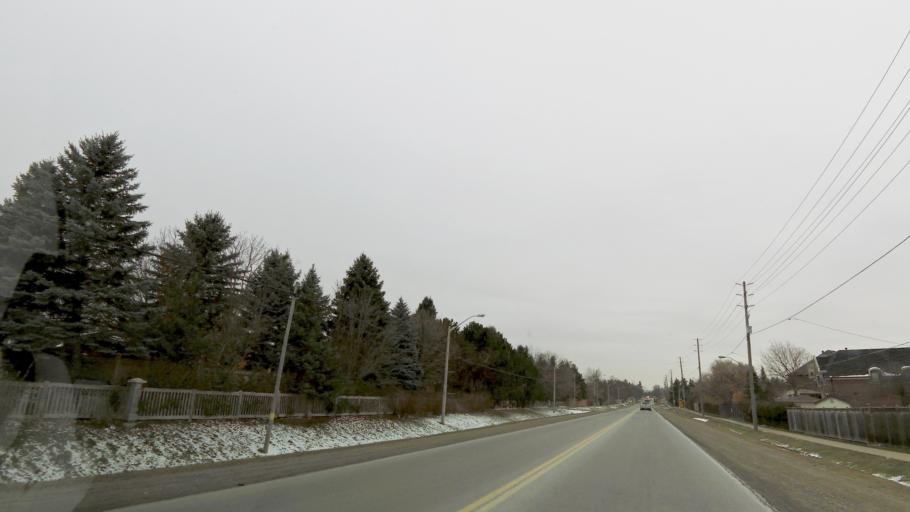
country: CA
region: Ontario
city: Vaughan
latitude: 43.8375
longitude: -79.6224
